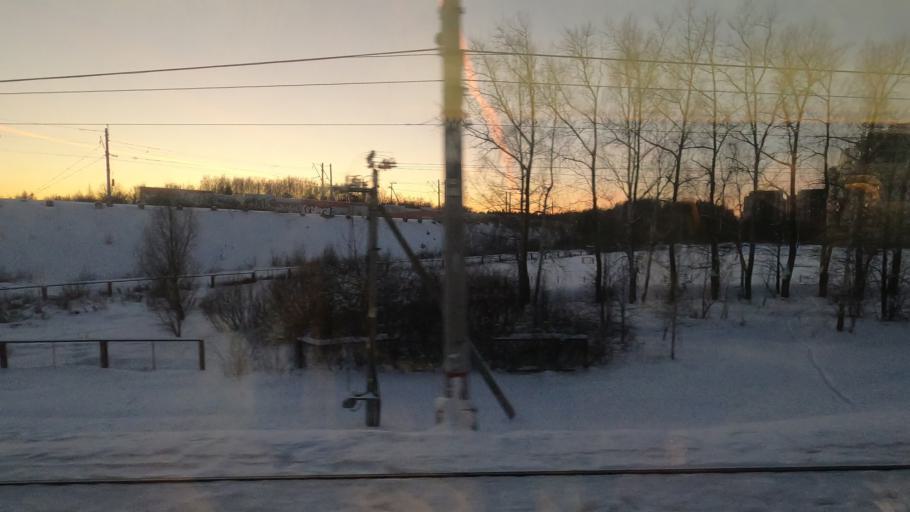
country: RU
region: Moskovskaya
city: Lobnya
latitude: 55.9991
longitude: 37.4917
